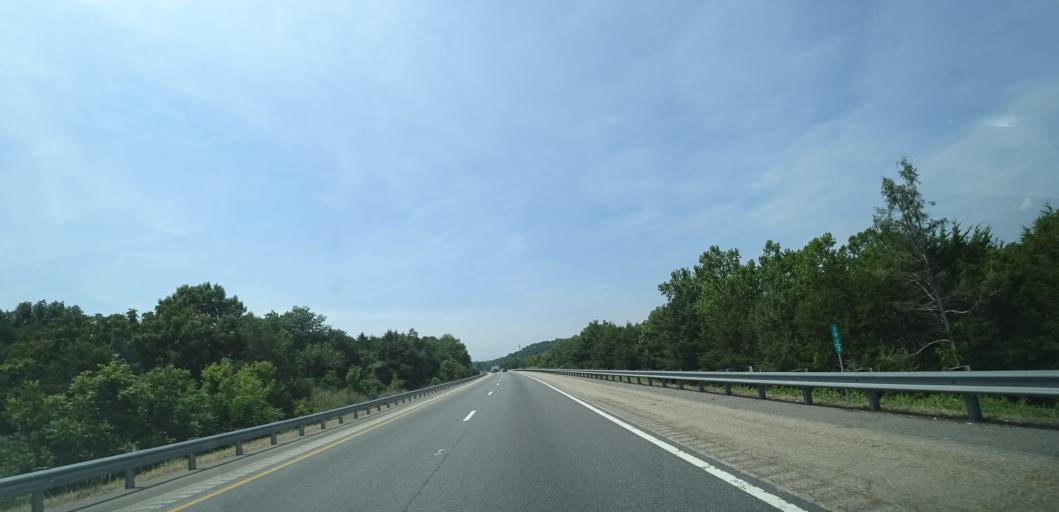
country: US
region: Virginia
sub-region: Rockbridge County
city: East Lexington
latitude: 37.7930
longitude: -79.3984
